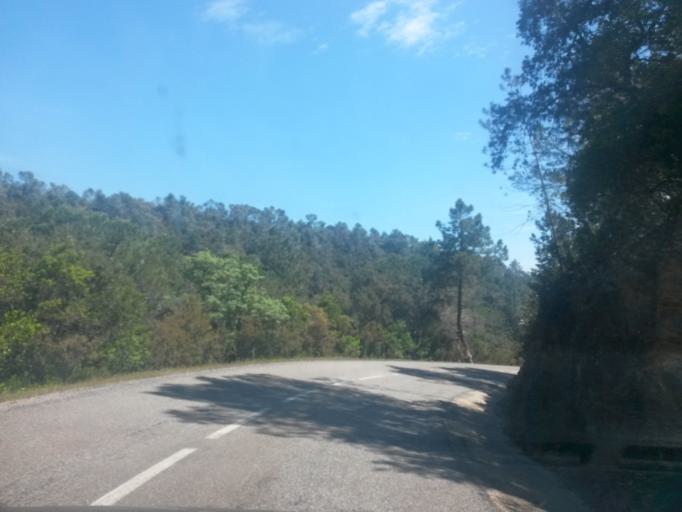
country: ES
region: Catalonia
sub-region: Provincia de Girona
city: Madremanya
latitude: 41.9832
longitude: 2.9412
